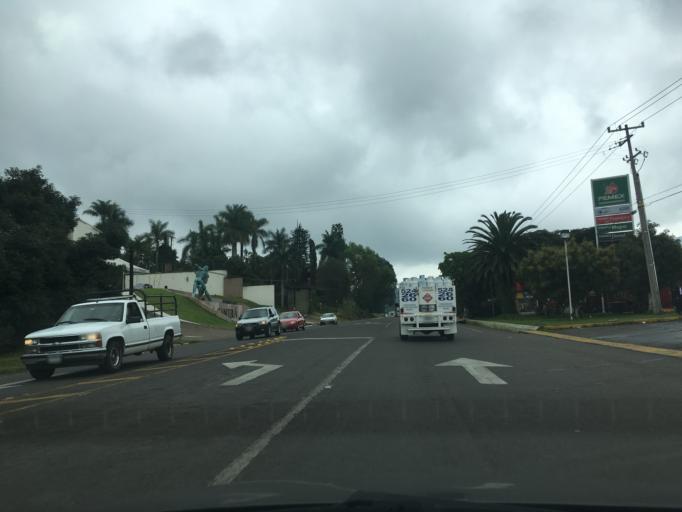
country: MX
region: Michoacan
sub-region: Uruapan
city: Toreo Bajo (El Toreo Bajo)
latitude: 19.4383
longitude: -102.0148
